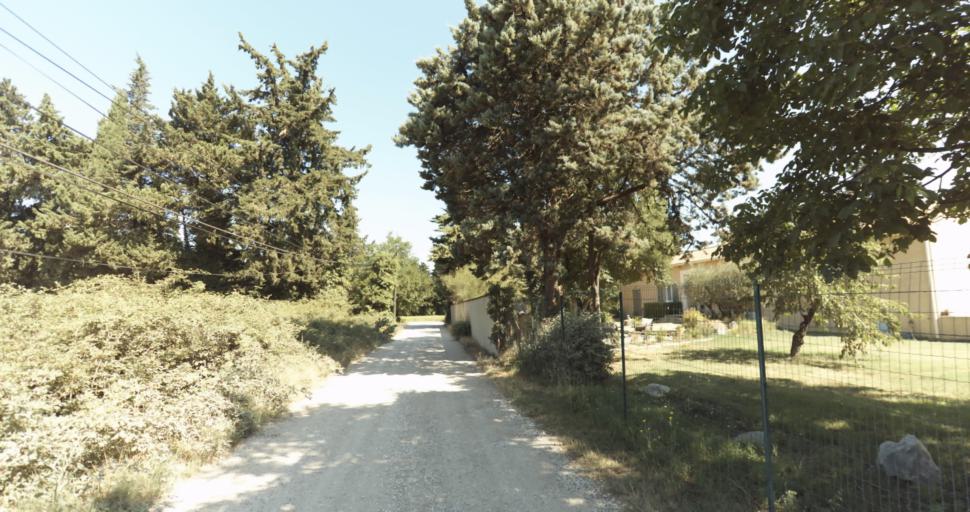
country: FR
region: Provence-Alpes-Cote d'Azur
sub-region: Departement du Vaucluse
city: Monteux
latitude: 44.0111
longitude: 5.0024
